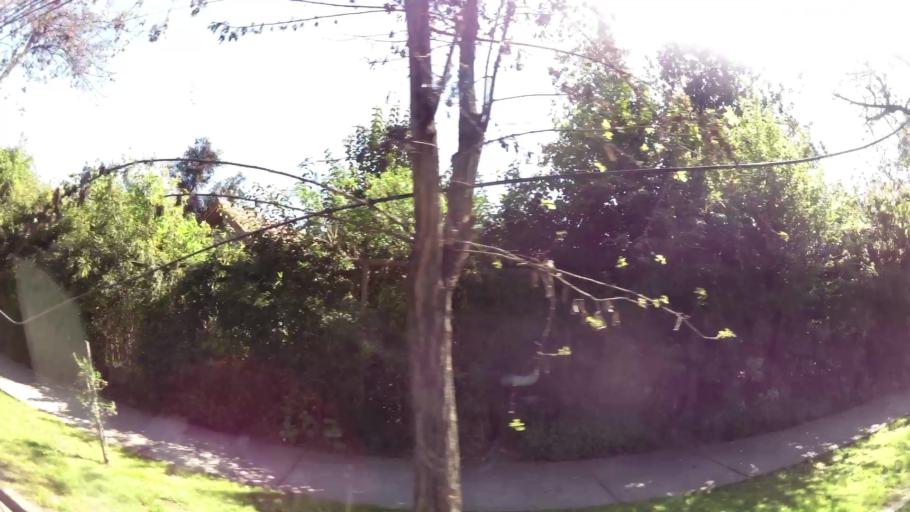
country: CL
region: Santiago Metropolitan
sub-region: Provincia de Santiago
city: Villa Presidente Frei, Nunoa, Santiago, Chile
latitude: -33.4383
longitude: -70.5223
